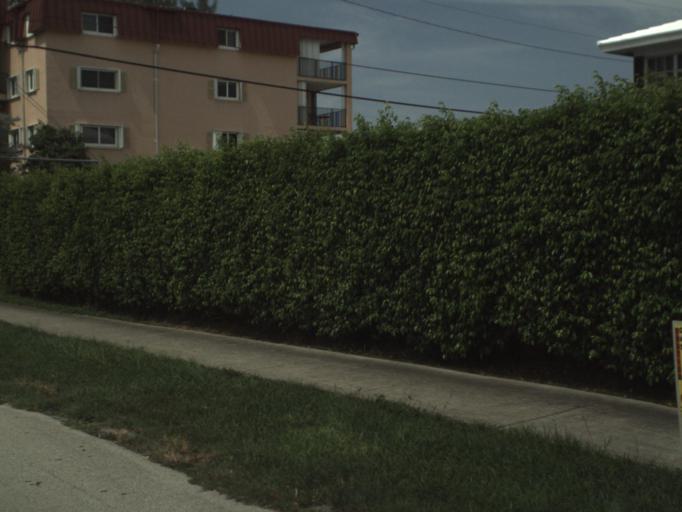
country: US
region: Florida
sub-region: Broward County
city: Hillsboro Beach
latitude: 26.3125
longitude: -80.0777
